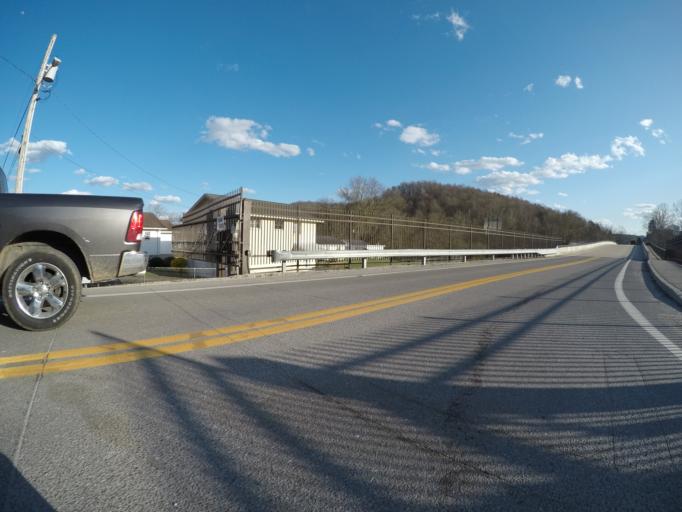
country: US
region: West Virginia
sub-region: Kanawha County
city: Charleston
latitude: 38.4003
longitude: -81.5786
